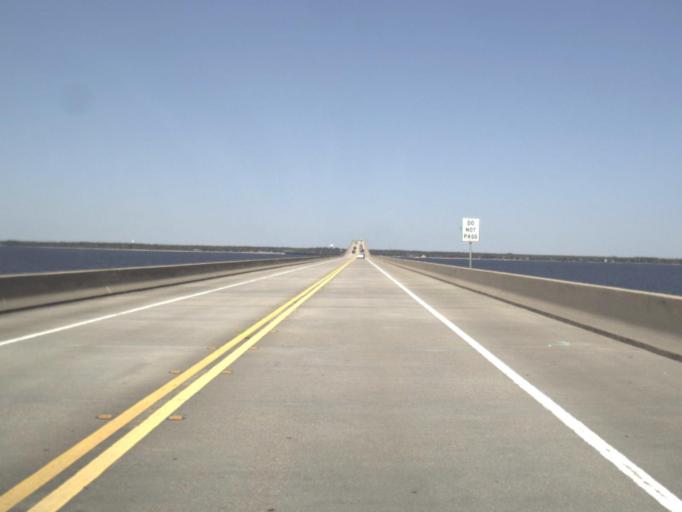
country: US
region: Florida
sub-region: Walton County
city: Miramar Beach
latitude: 30.4222
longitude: -86.4205
